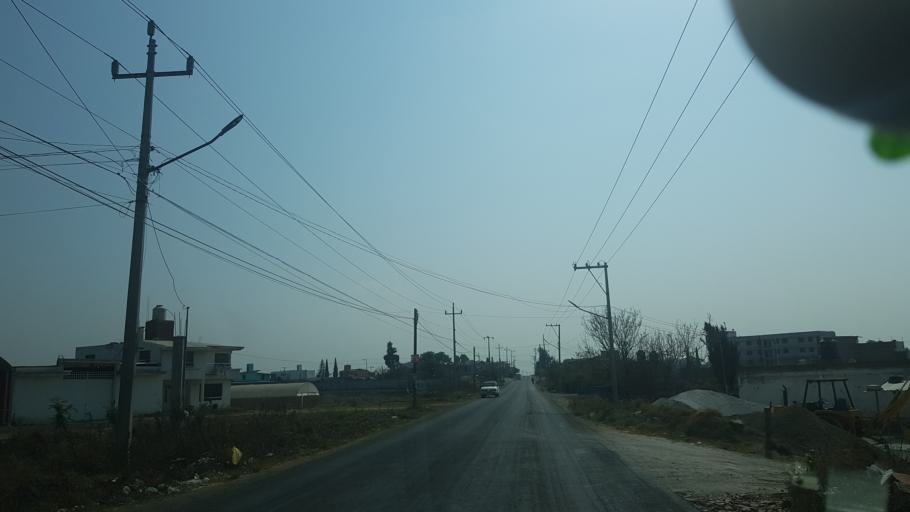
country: MX
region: Puebla
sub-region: San Jeronimo Tecuanipan
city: Los Reyes Tlanechicolpan
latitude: 19.0536
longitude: -98.3395
